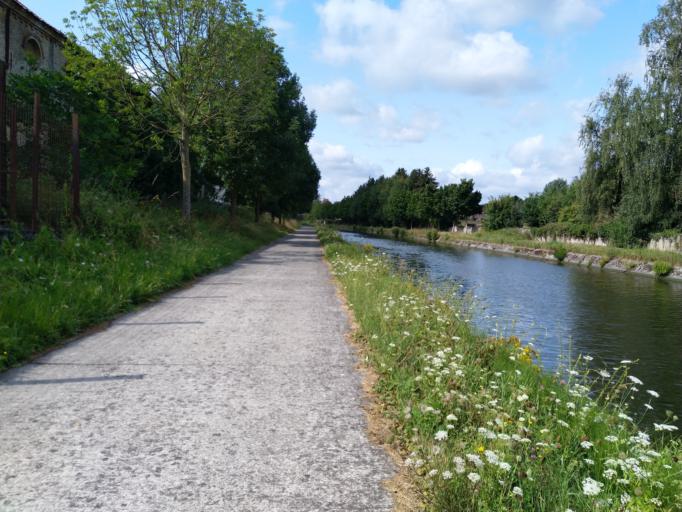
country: BE
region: Wallonia
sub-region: Province du Hainaut
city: Bernissart
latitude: 50.4983
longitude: 3.6608
